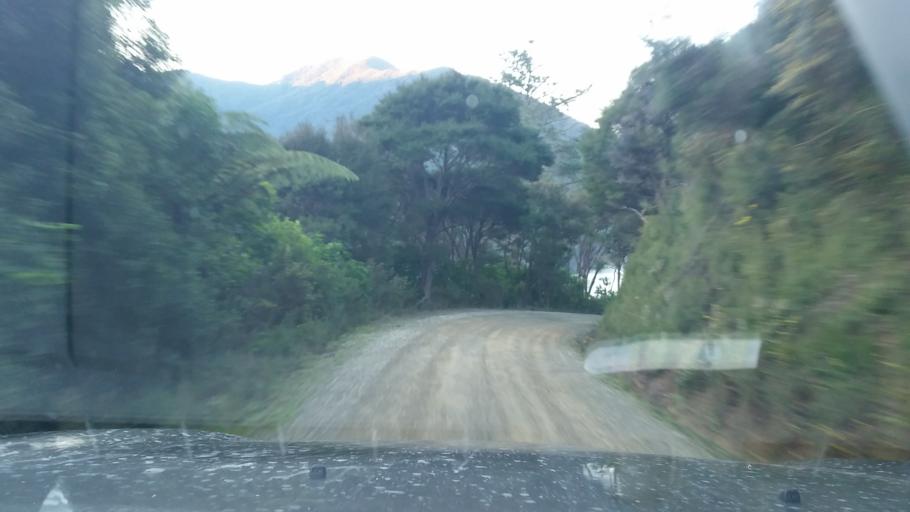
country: NZ
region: Marlborough
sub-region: Marlborough District
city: Picton
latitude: -41.1309
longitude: 174.1500
